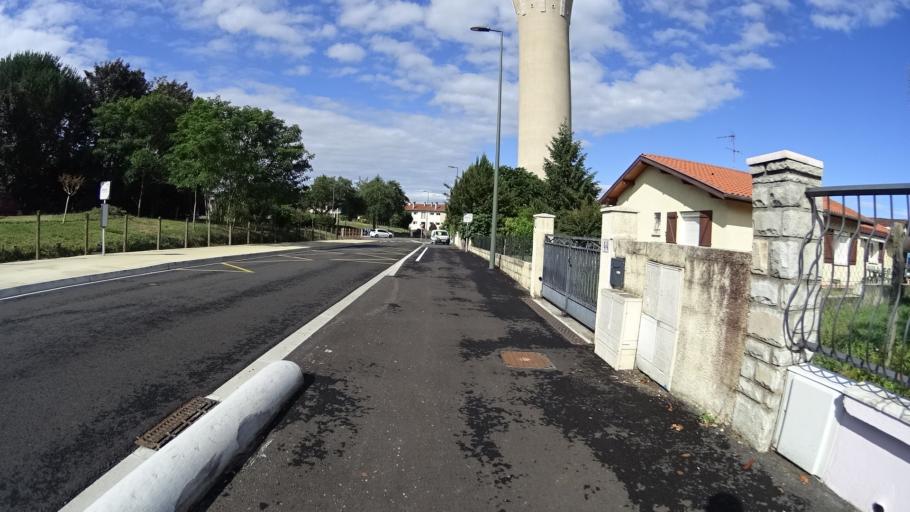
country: FR
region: Aquitaine
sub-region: Departement des Landes
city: Dax
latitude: 43.6984
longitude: -1.0722
